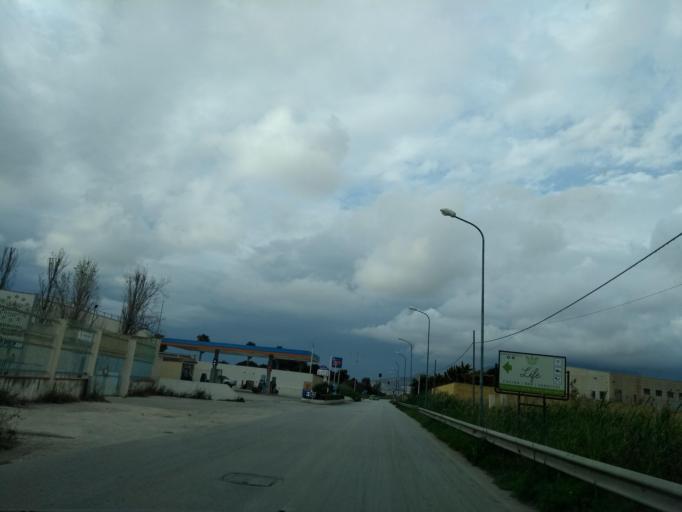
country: IT
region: Sicily
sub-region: Trapani
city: Paceco
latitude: 37.9824
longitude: 12.5311
